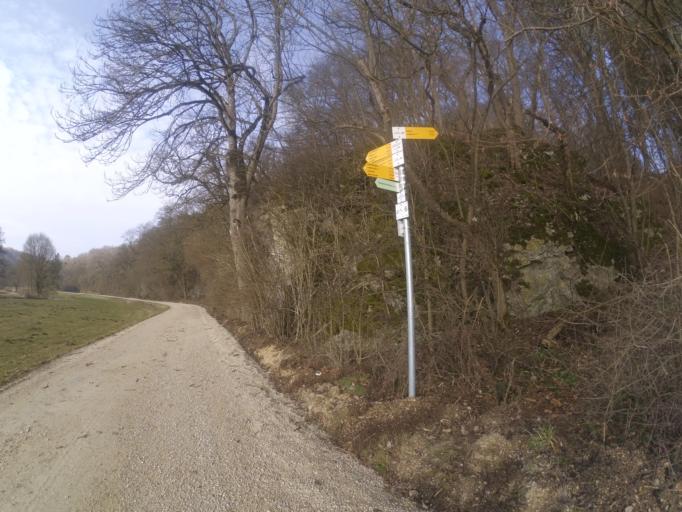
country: DE
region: Baden-Wuerttemberg
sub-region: Tuebingen Region
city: Rechtenstein
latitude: 48.2698
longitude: 9.5389
